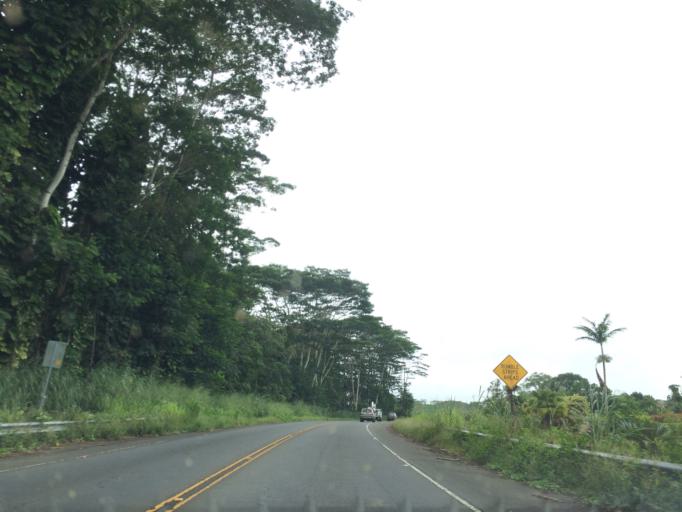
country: US
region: Hawaii
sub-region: Hawaii County
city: Nanawale Estates
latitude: 19.4948
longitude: -154.9408
